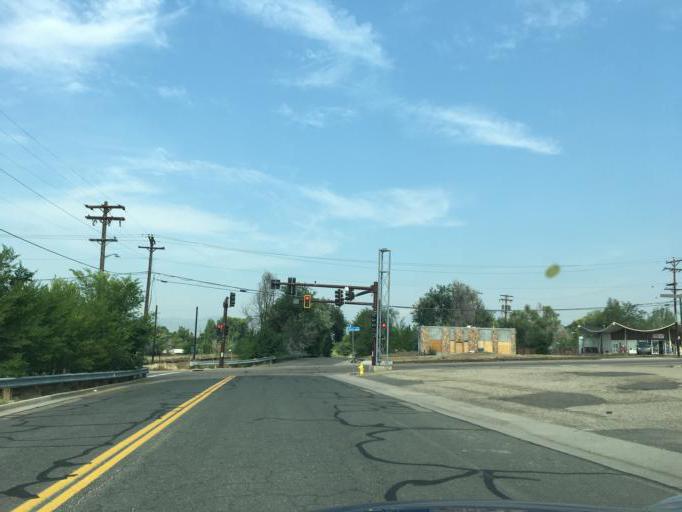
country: US
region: Colorado
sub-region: Jefferson County
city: Arvada
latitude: 39.8099
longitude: -105.0901
